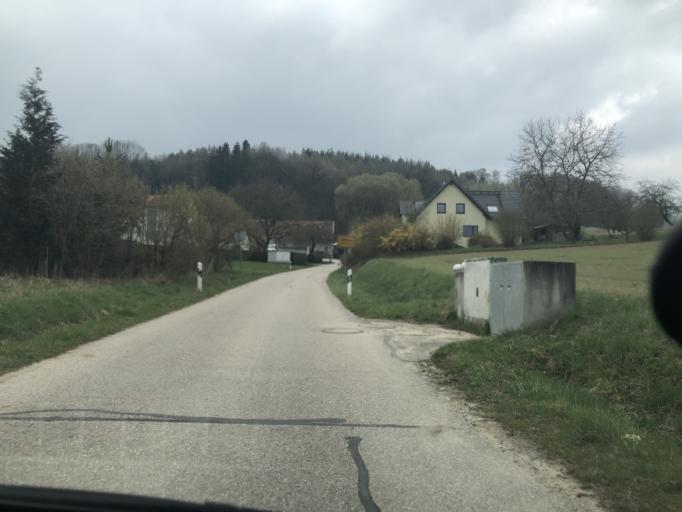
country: DE
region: Bavaria
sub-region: Upper Bavaria
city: Wolfersdorf
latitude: 48.4412
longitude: 11.7120
